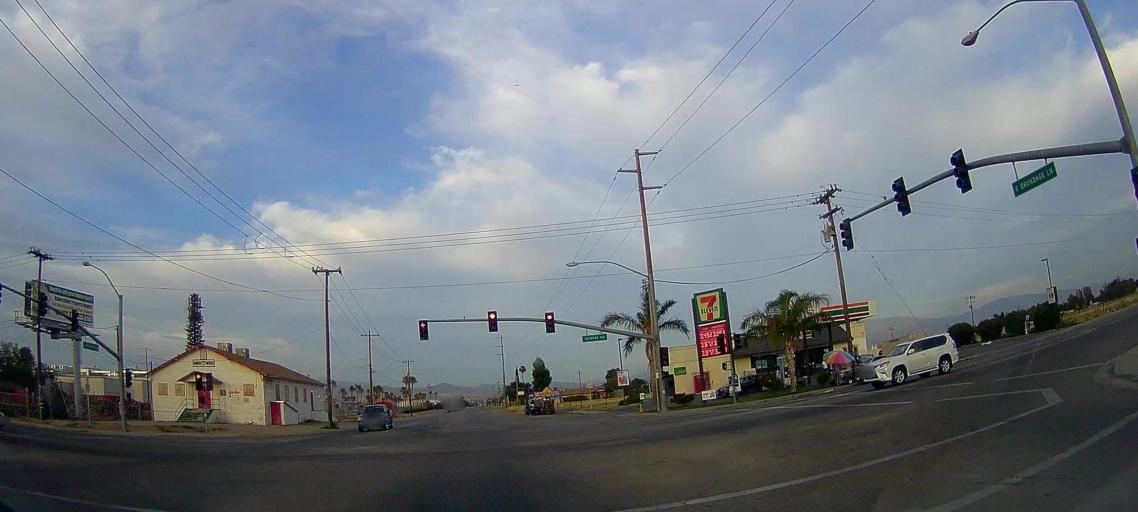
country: US
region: California
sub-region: Kern County
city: Bakersfield
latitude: 35.3543
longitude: -118.9323
